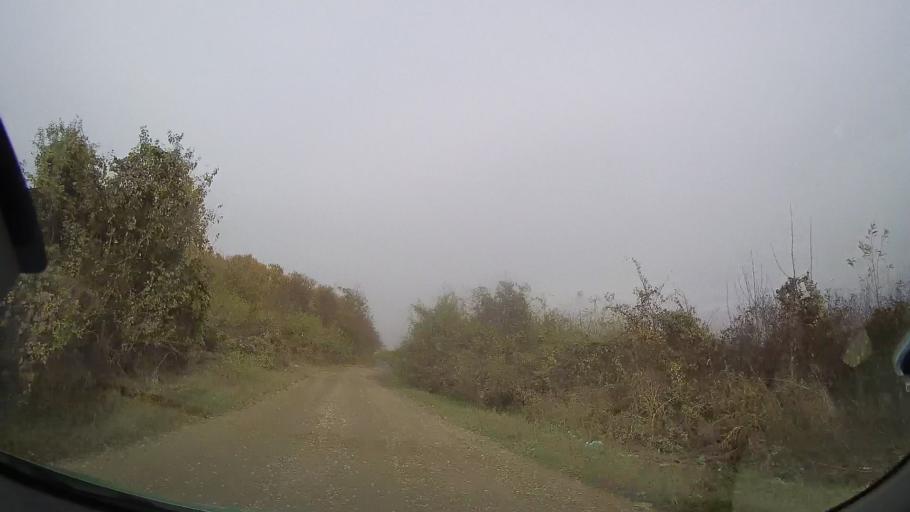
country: RO
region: Prahova
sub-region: Comuna Gorgota
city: Potigrafu
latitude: 44.7506
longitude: 26.1237
